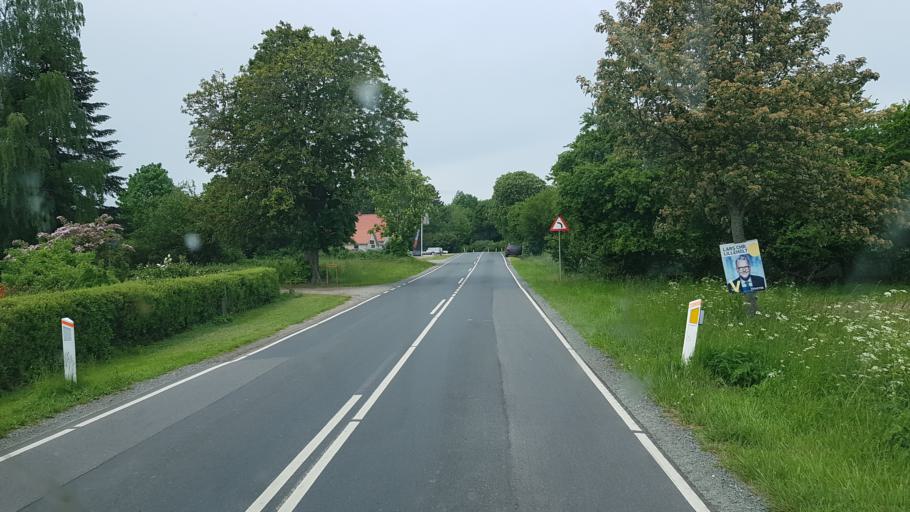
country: DK
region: South Denmark
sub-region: Nordfyns Kommune
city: Sonderso
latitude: 55.5716
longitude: 10.1993
